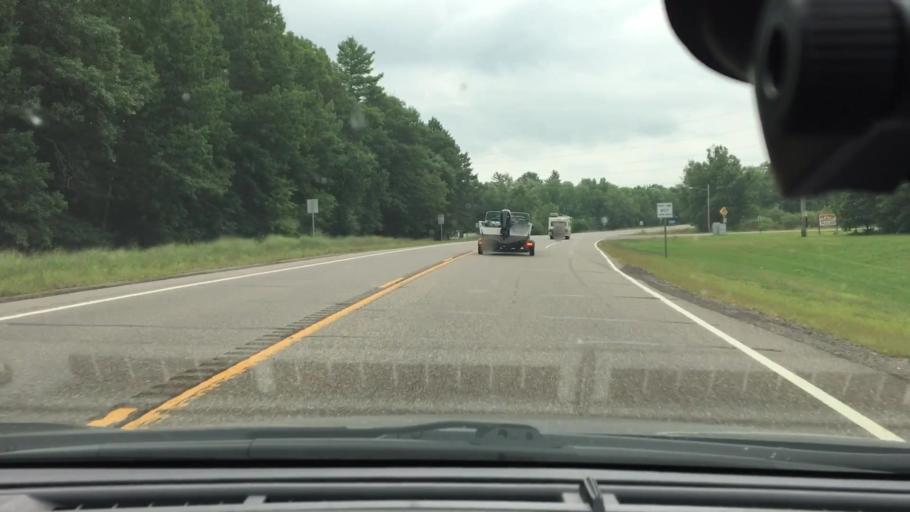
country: US
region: Minnesota
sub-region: Crow Wing County
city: Crosby
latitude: 46.5418
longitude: -93.9522
